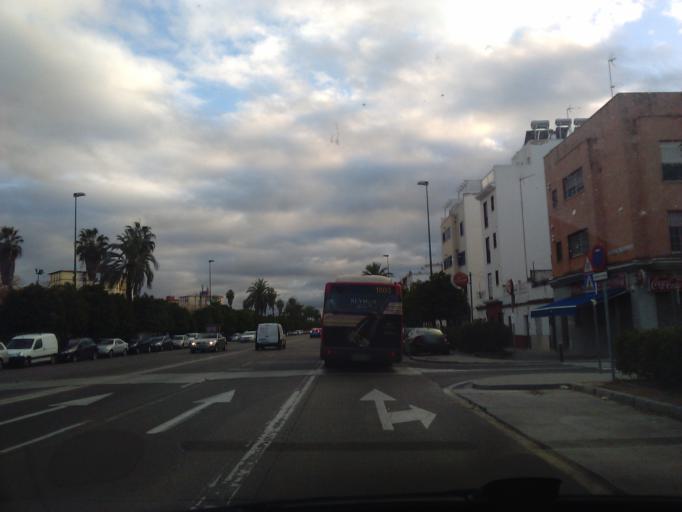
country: ES
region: Andalusia
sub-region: Provincia de Sevilla
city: Sevilla
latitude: 37.3851
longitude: -5.9598
